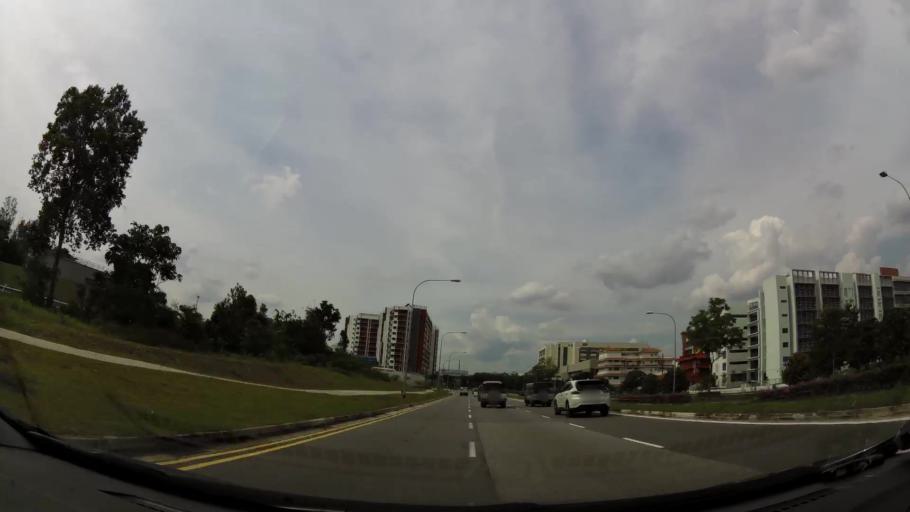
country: MY
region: Johor
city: Johor Bahru
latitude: 1.4596
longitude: 103.8109
